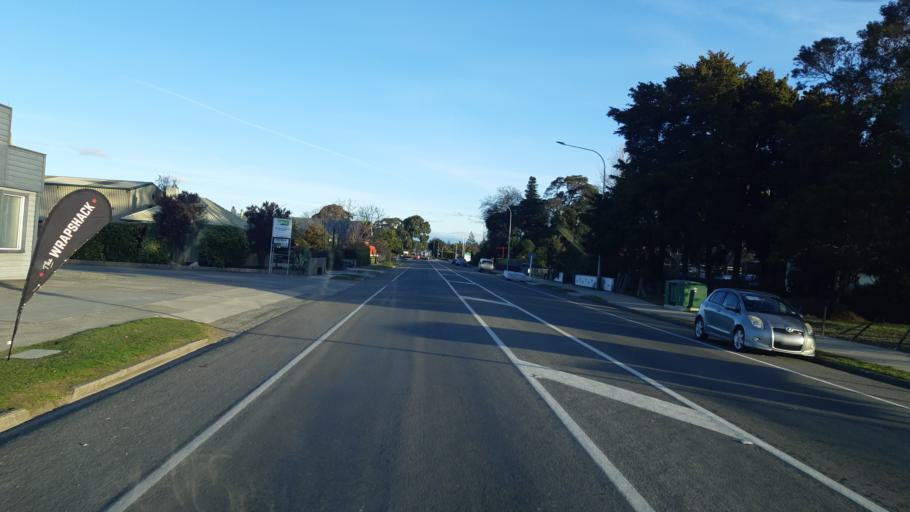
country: NZ
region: Tasman
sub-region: Tasman District
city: Motueka
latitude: -41.1305
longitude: 173.0101
